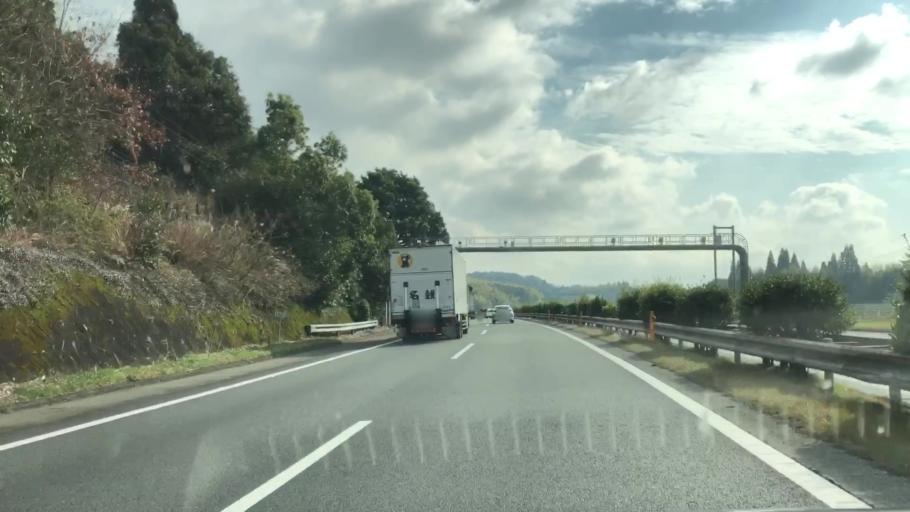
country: JP
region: Fukuoka
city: Setakamachi-takayanagi
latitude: 33.0885
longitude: 130.5397
